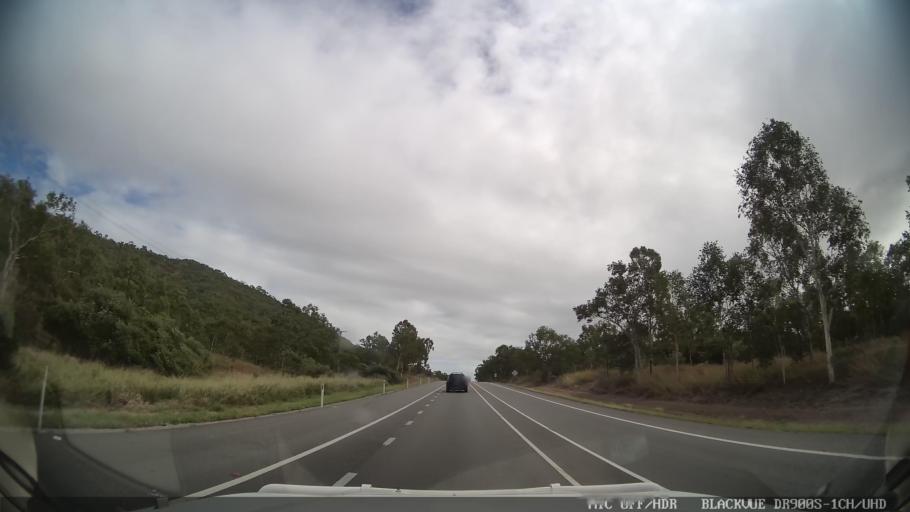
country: AU
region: Queensland
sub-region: Townsville
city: Townsville
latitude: -19.3671
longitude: 146.8921
